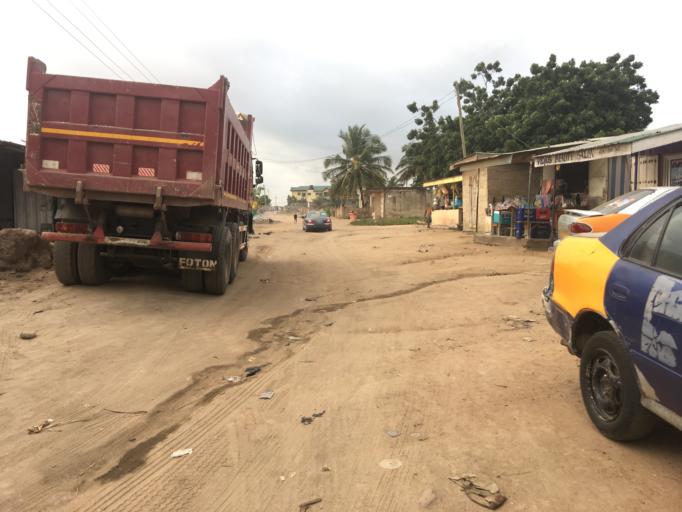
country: GH
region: Central
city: Kasoa
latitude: 5.5391
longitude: -0.4022
